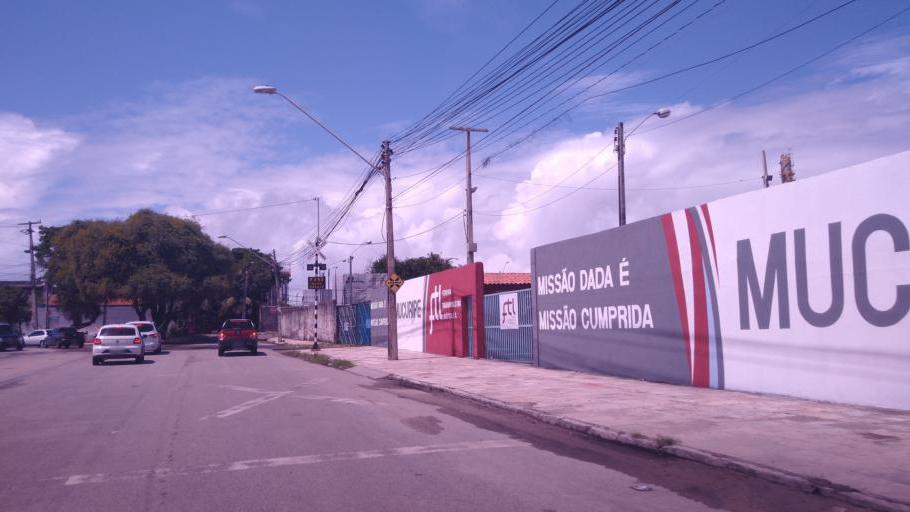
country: BR
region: Ceara
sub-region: Fortaleza
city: Fortaleza
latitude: -3.7142
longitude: -38.4727
